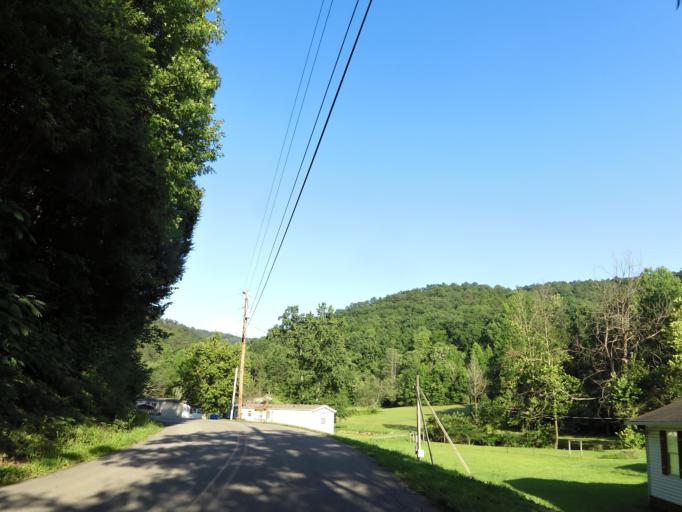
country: US
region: Tennessee
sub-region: Blount County
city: Maryville
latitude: 35.6938
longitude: -83.9014
